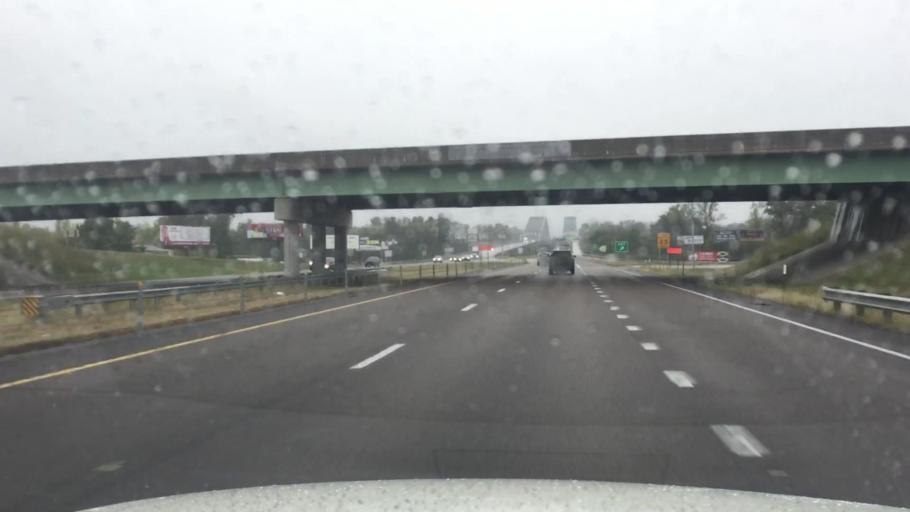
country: US
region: Missouri
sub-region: Cole County
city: Jefferson City
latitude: 38.5954
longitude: -92.1713
